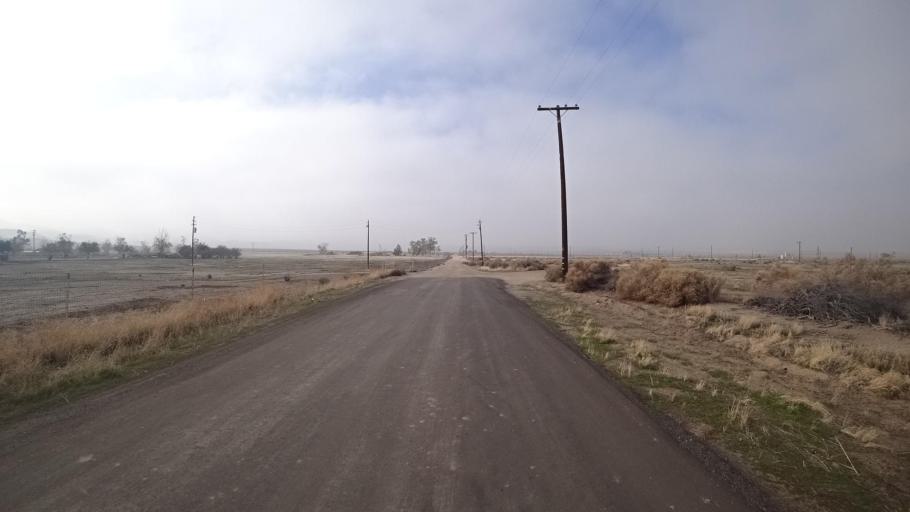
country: US
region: California
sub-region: Kern County
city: Maricopa
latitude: 35.0469
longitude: -119.3547
